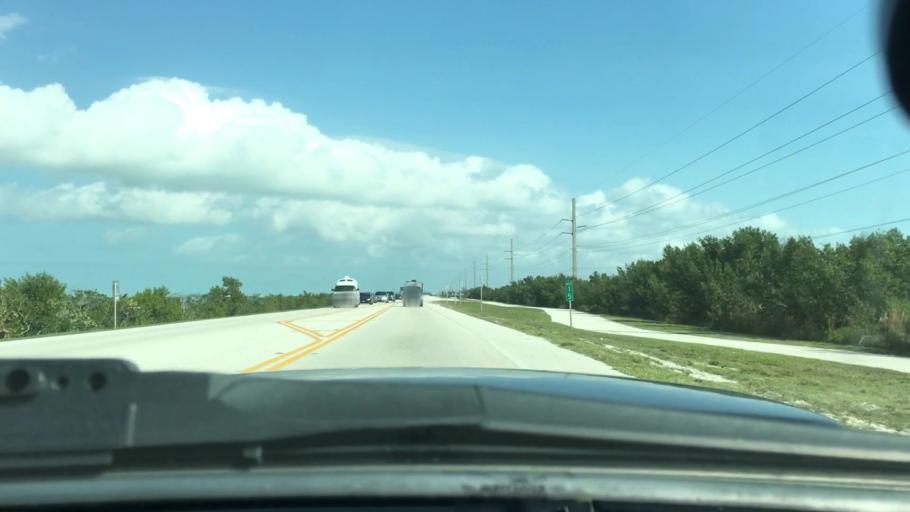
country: US
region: Florida
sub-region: Monroe County
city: Big Coppitt Key
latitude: 24.6299
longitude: -81.5917
